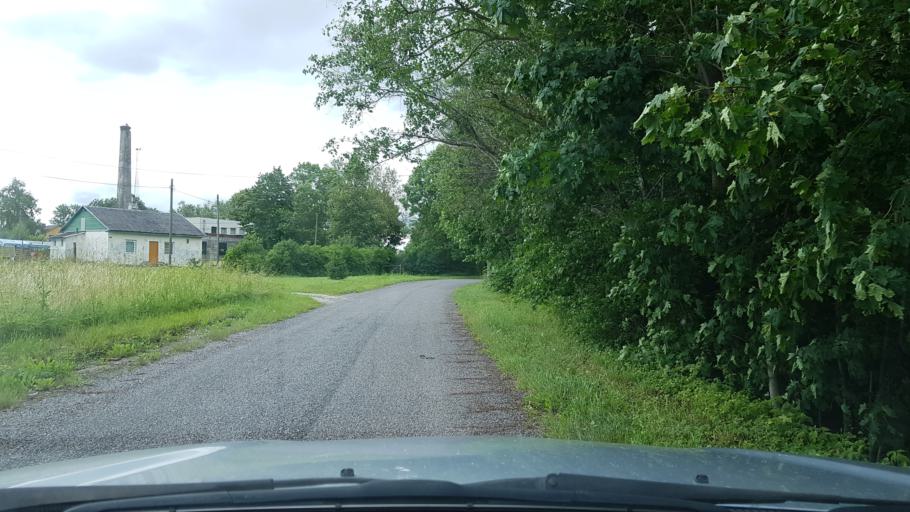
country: EE
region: Ida-Virumaa
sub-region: Sillamaee linn
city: Sillamae
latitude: 59.3749
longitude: 27.7622
